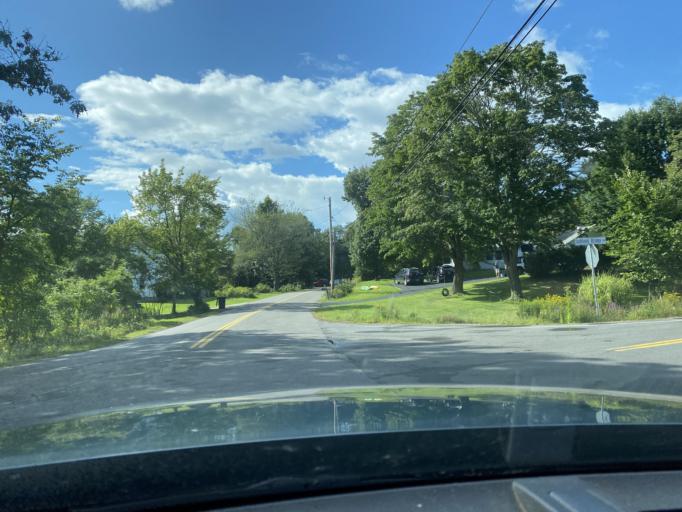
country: US
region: Maine
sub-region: York County
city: Kittery
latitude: 43.1462
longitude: -70.7128
